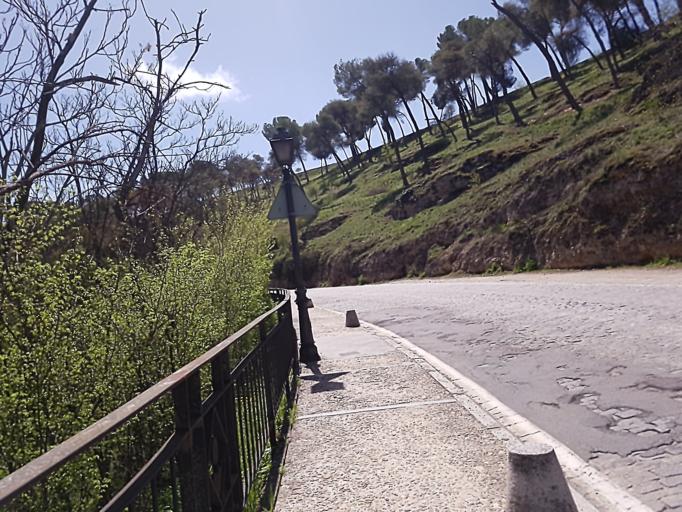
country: ES
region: Castille and Leon
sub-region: Provincia de Segovia
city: Segovia
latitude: 40.9502
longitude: -4.1308
